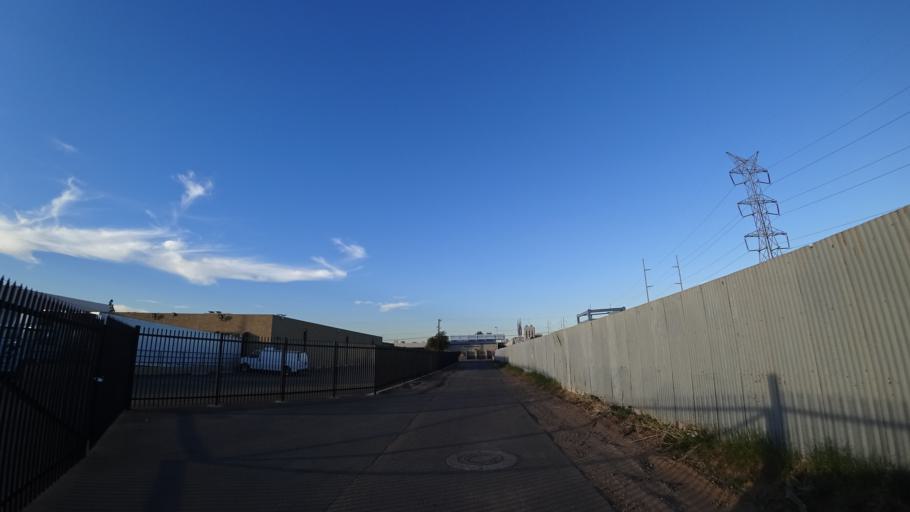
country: US
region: Arizona
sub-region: Maricopa County
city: Phoenix
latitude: 33.4250
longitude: -112.0792
